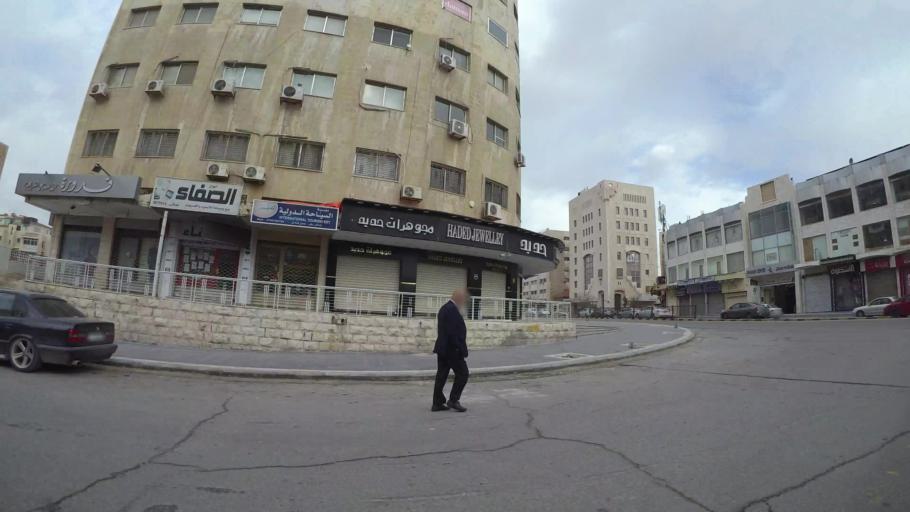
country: JO
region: Amman
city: Amman
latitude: 31.9690
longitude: 35.9154
